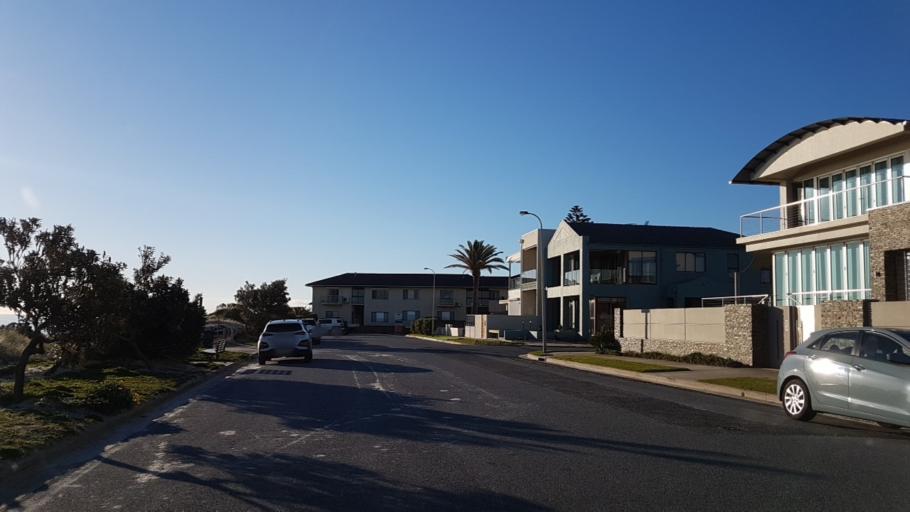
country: AU
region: South Australia
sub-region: Charles Sturt
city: Grange
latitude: -34.8858
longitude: 138.4843
